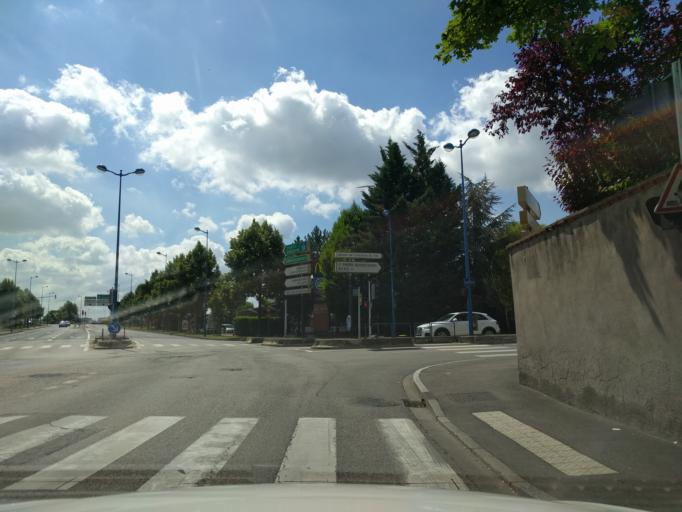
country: FR
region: Lorraine
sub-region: Departement de Meurthe-et-Moselle
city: Jarville-la-Malgrange
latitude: 48.6797
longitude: 6.1986
